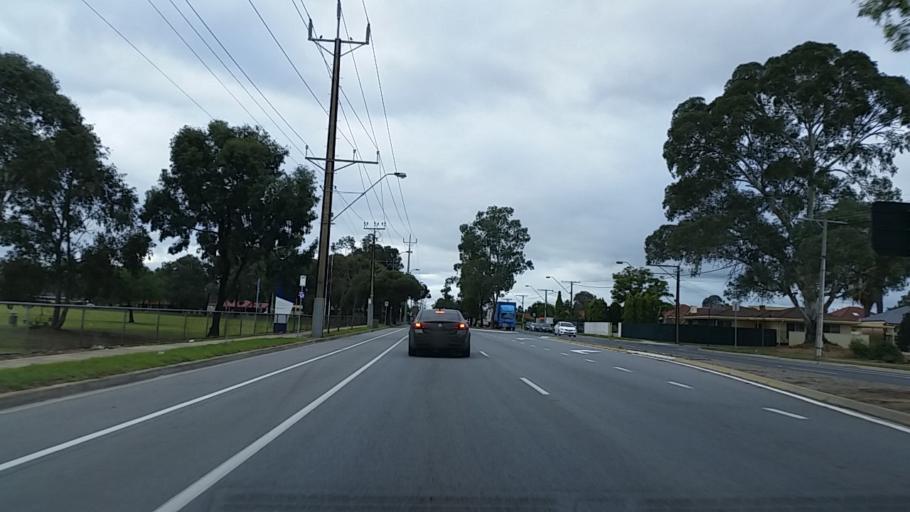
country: AU
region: South Australia
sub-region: Salisbury
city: Salisbury
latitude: -34.7867
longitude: 138.6196
